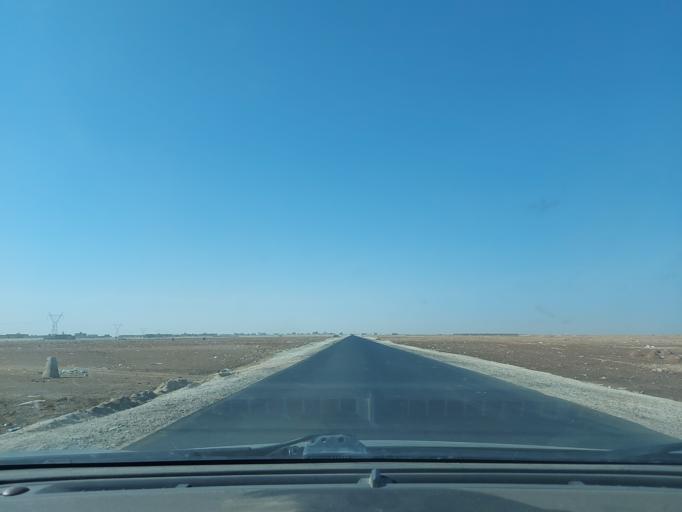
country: MR
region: Nouakchott
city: Nouakchott
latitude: 18.0066
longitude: -15.9881
